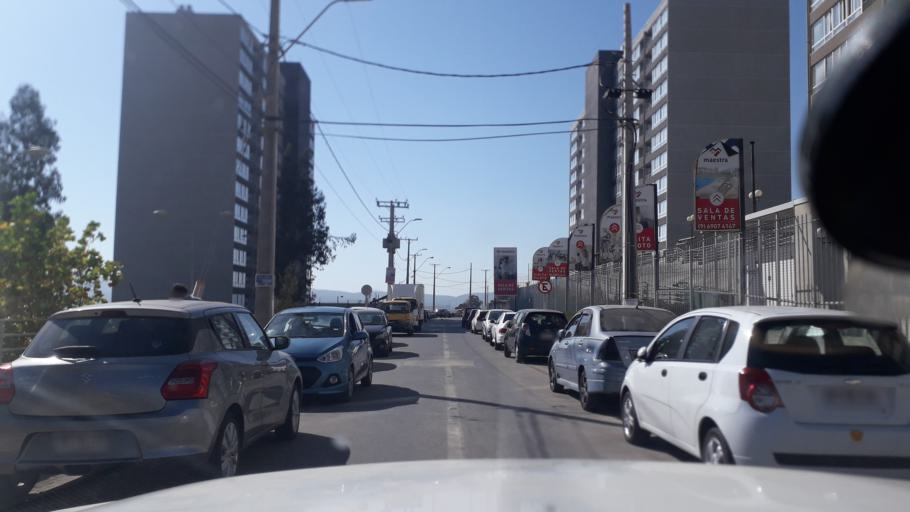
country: CL
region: Valparaiso
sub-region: Provincia de Marga Marga
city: Quilpue
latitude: -33.0681
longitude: -71.4127
